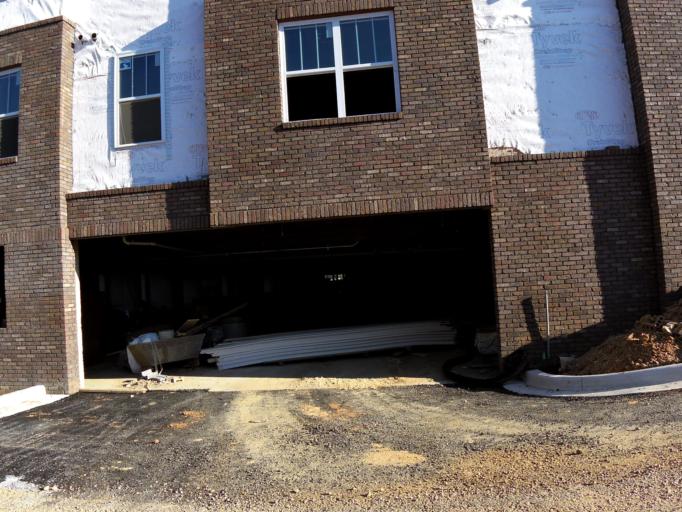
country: US
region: Tennessee
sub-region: Knox County
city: Knoxville
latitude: 35.9673
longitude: -83.9058
